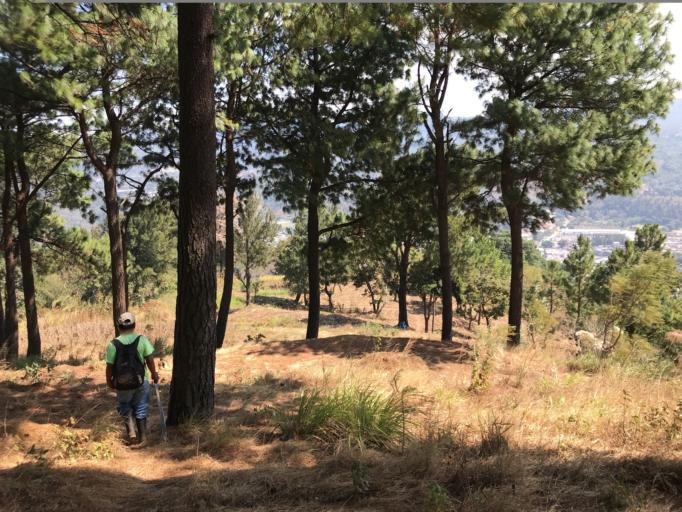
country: GT
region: Guatemala
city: Villa Canales
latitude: 14.4801
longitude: -90.5447
